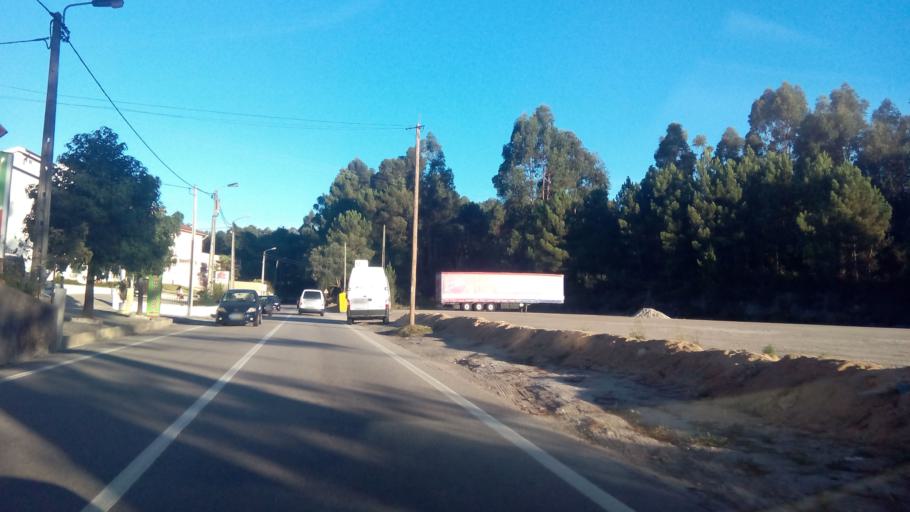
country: PT
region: Porto
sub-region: Paredes
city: Baltar
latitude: 41.1786
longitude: -8.3870
